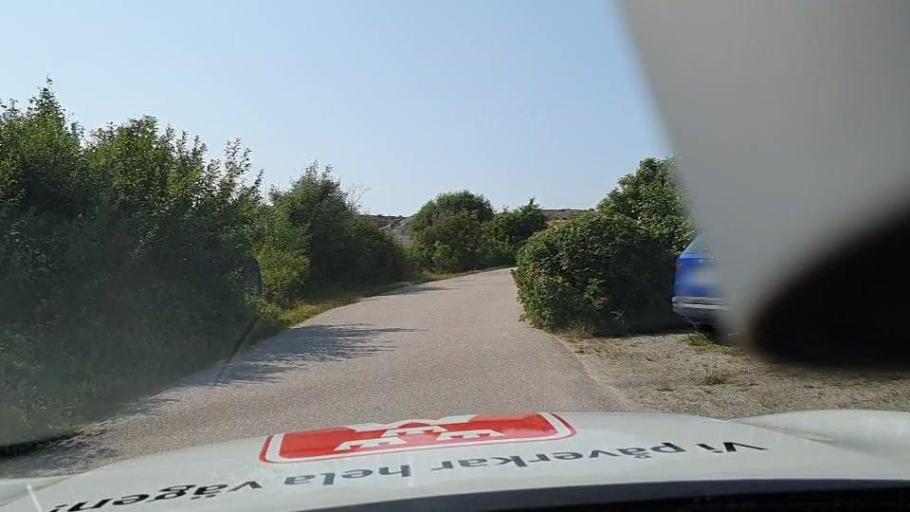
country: SE
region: Vaestra Goetaland
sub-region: Lysekils Kommun
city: Lysekil
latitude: 58.1189
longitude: 11.4505
